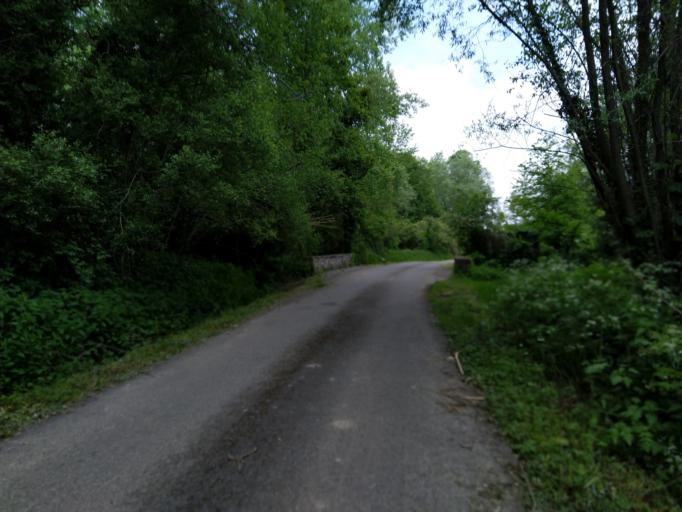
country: BE
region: Wallonia
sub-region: Province du Hainaut
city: Lens
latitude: 50.5715
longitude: 3.9234
